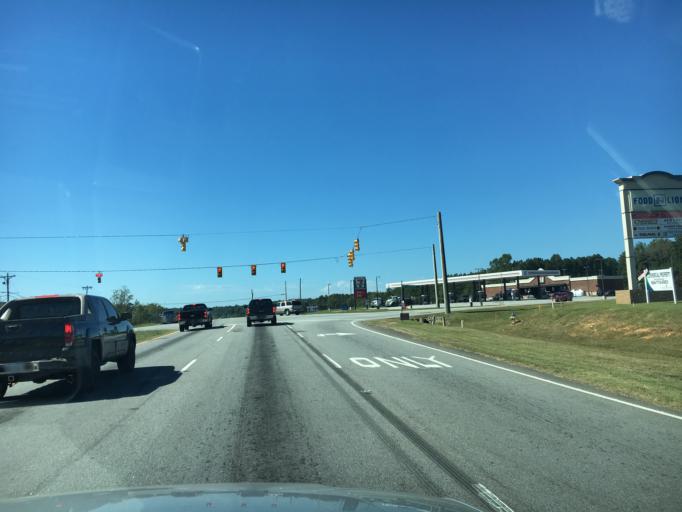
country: US
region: South Carolina
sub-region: Pickens County
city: Clemson
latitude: 34.6952
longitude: -82.8776
